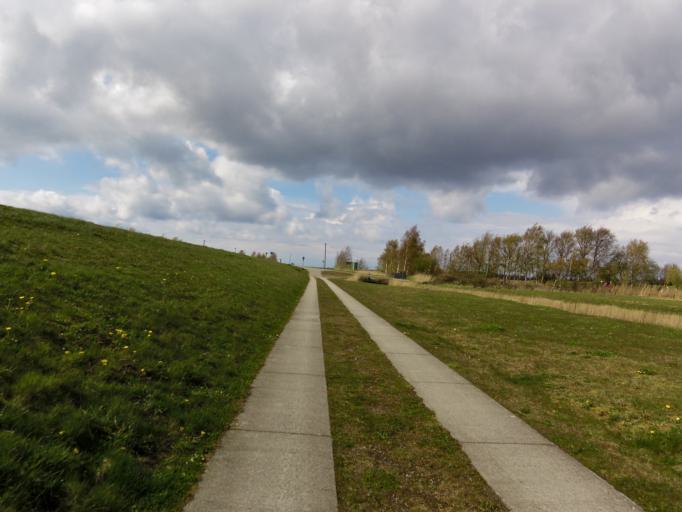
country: DE
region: Mecklenburg-Vorpommern
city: Zingst
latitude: 54.4236
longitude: 12.7313
